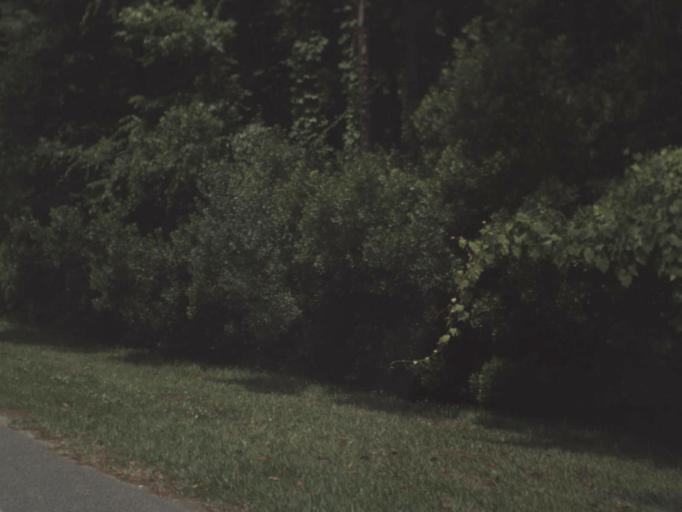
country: US
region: Florida
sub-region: Nassau County
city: Yulee
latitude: 30.6852
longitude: -81.6517
